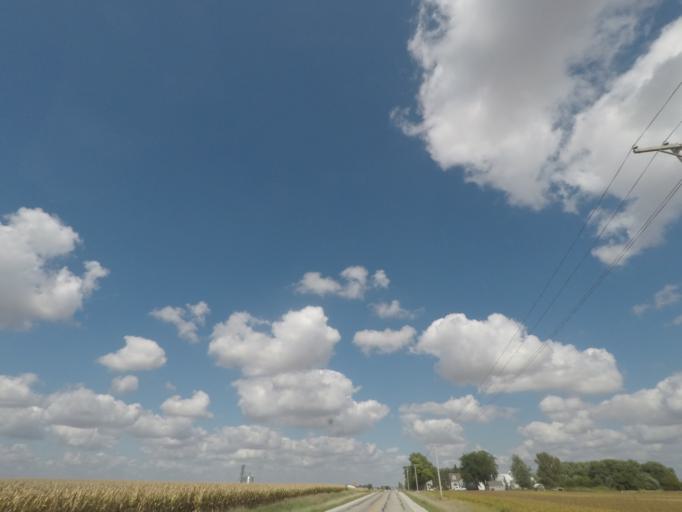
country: US
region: Iowa
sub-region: Story County
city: Nevada
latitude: 42.0420
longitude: -93.4057
